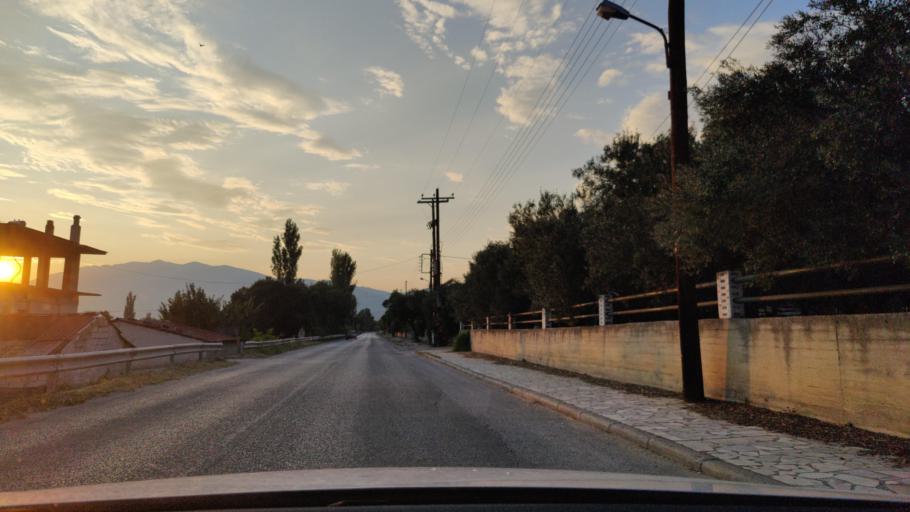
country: GR
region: Central Macedonia
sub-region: Nomos Serron
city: Sidirokastro
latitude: 41.2423
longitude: 23.3846
